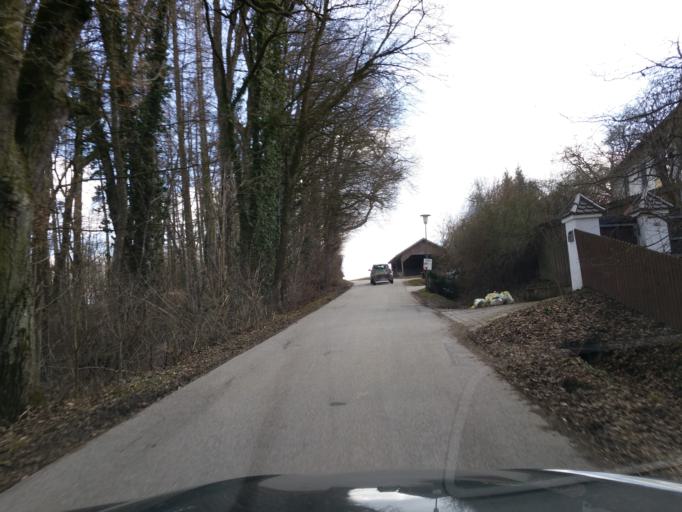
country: DE
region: Bavaria
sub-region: Lower Bavaria
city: Eching
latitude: 48.4912
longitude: 12.0395
